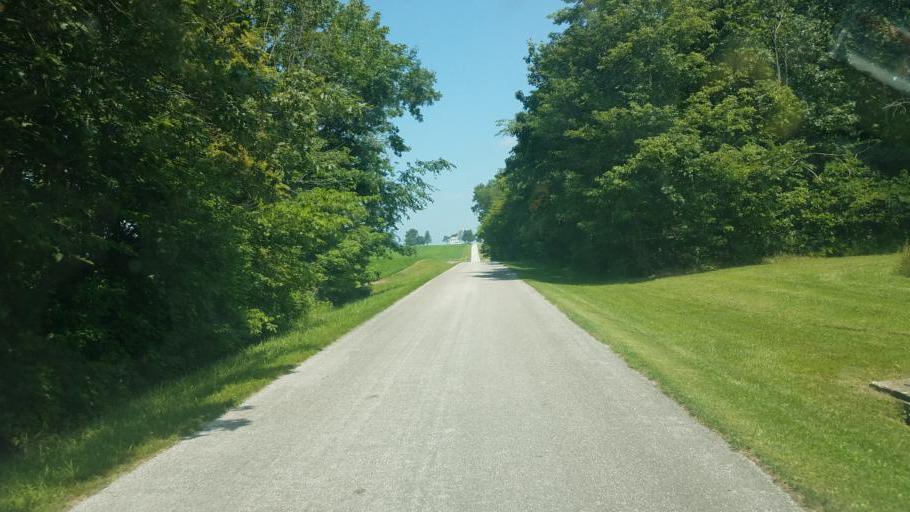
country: US
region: Ohio
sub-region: Sandusky County
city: Green Springs
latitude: 41.1173
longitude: -82.9766
